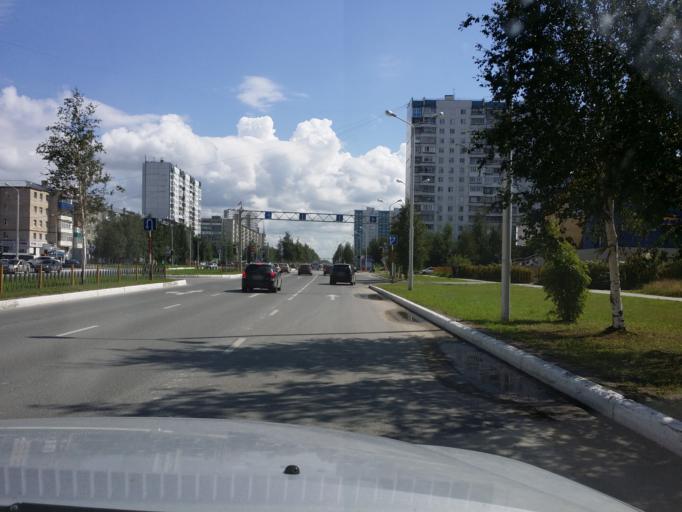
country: RU
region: Khanty-Mansiyskiy Avtonomnyy Okrug
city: Nizhnevartovsk
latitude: 60.9329
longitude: 76.5969
